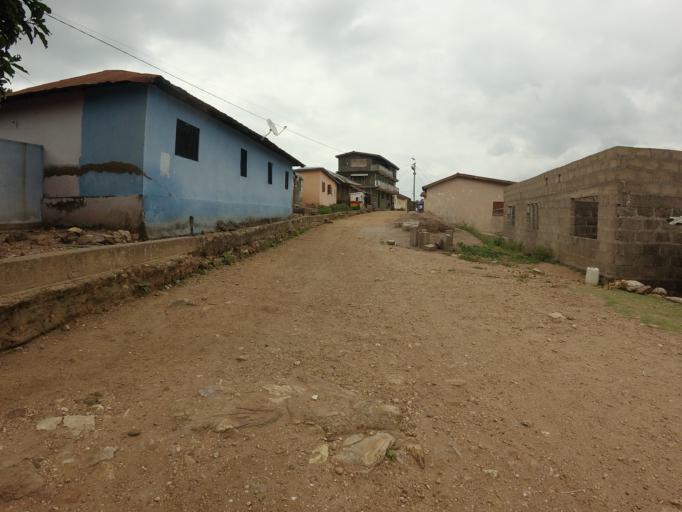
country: TG
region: Plateaux
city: Kpalime
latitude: 6.8604
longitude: 0.4406
